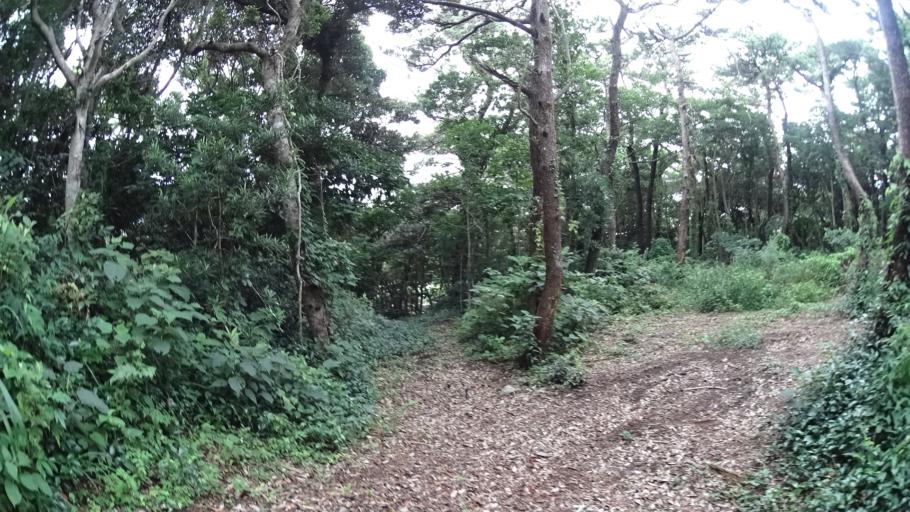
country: JP
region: Shizuoka
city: Shimoda
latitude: 34.3240
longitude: 139.2132
